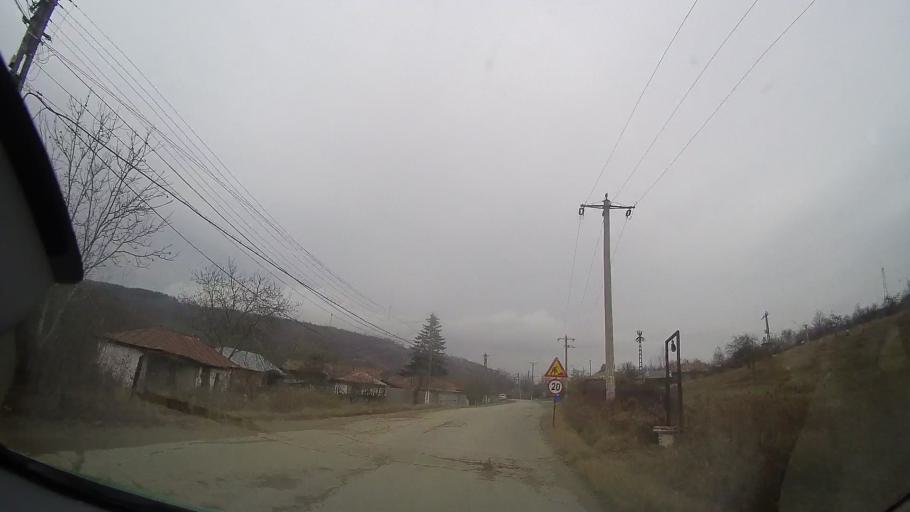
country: RO
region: Prahova
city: Ceptura de Sus
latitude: 45.0455
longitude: 26.3054
